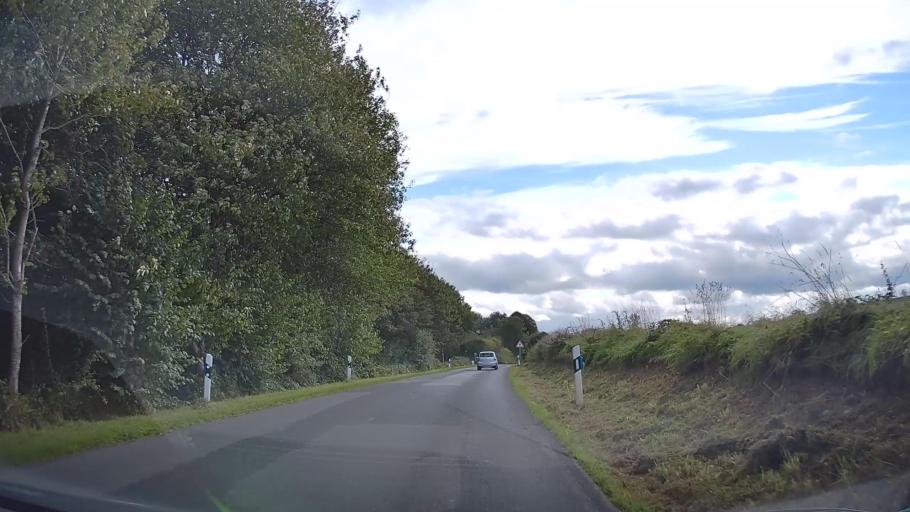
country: DE
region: Schleswig-Holstein
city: Ringsberg
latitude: 54.8364
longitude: 9.5892
